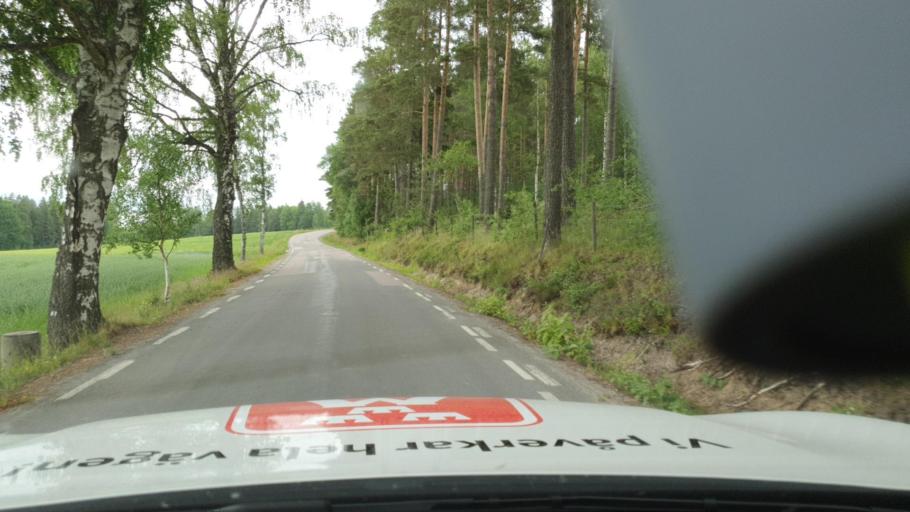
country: SE
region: Vaestra Goetaland
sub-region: Tidaholms Kommun
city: Olofstorp
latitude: 58.2450
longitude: 14.0978
